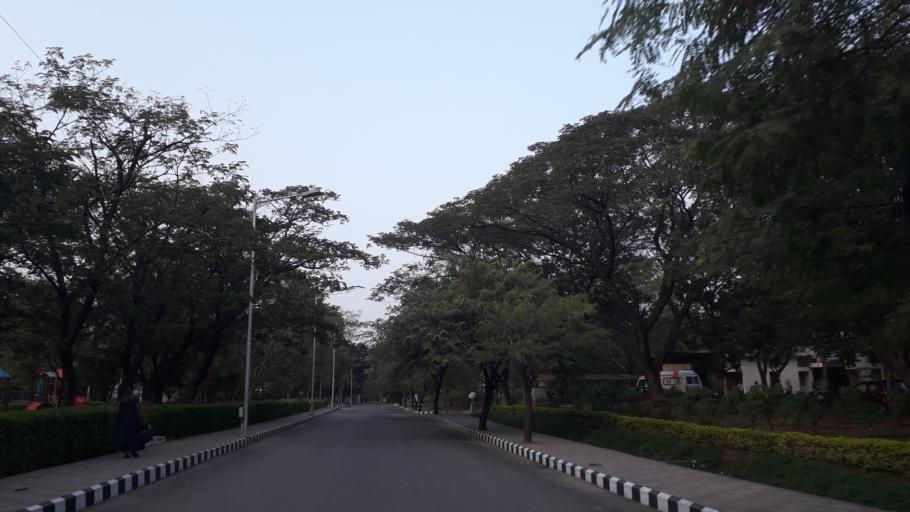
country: IN
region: Telangana
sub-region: Rangareddi
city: Singapur
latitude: 17.4693
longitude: 78.1647
